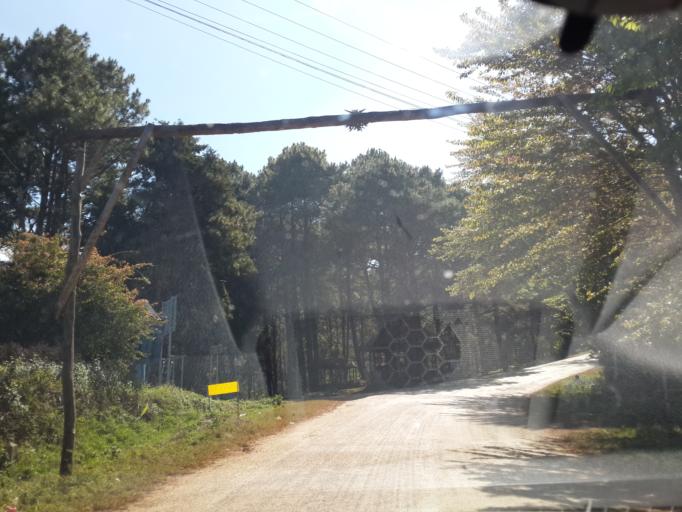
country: TH
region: Chiang Mai
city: Fang
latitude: 19.9314
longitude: 99.0428
